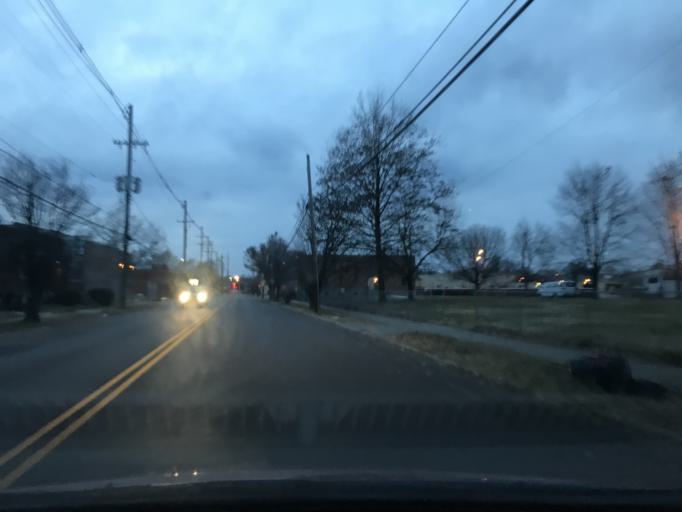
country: US
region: Kentucky
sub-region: Jefferson County
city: Audubon Park
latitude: 38.2258
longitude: -85.7471
